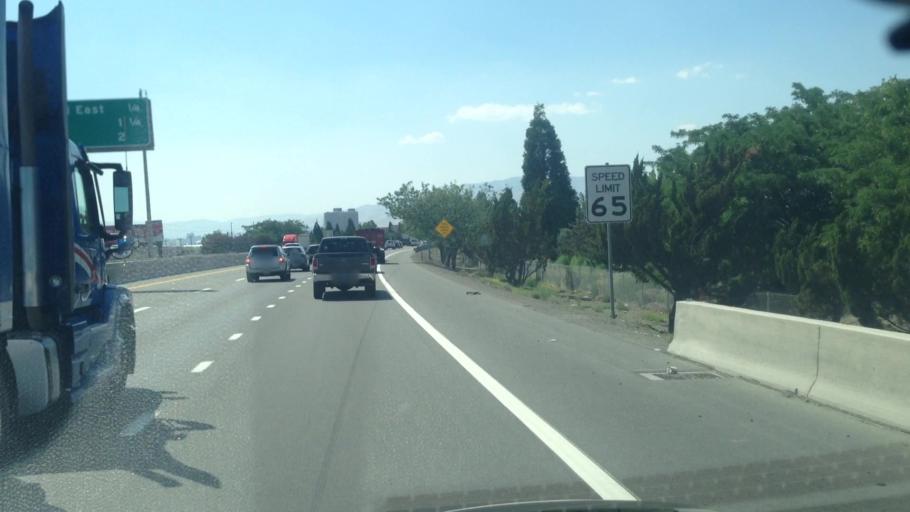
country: US
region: Nevada
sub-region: Washoe County
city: Sparks
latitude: 39.5295
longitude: -119.7272
